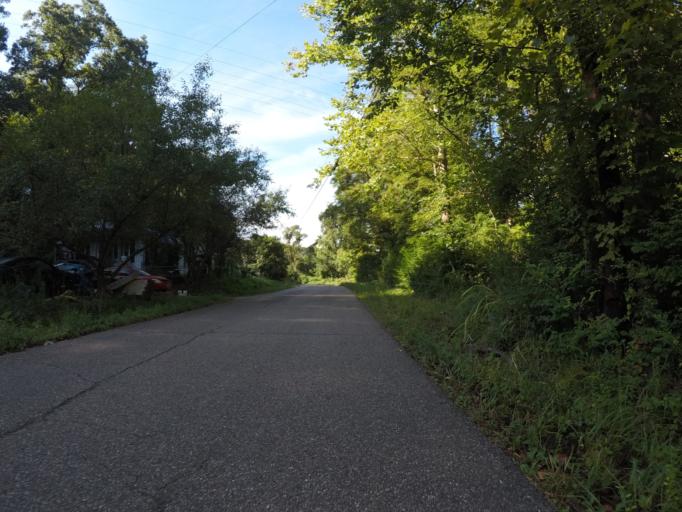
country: US
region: West Virginia
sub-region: Cabell County
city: Huntington
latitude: 38.4716
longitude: -82.4602
